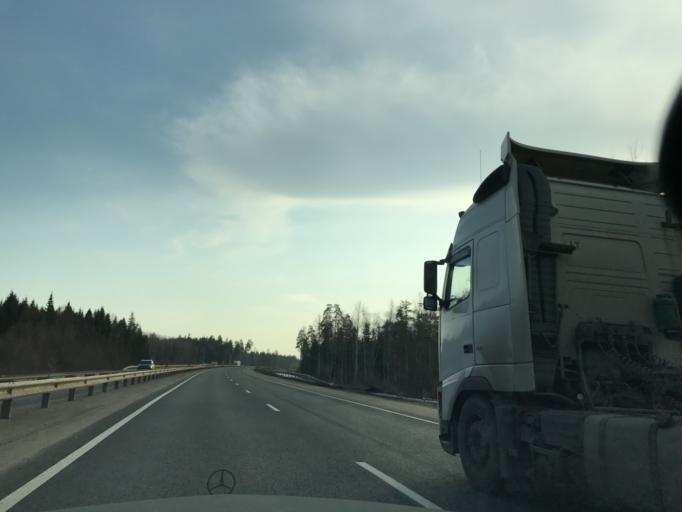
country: RU
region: Vladimir
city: Kameshkovo
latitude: 56.1780
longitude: 40.9459
